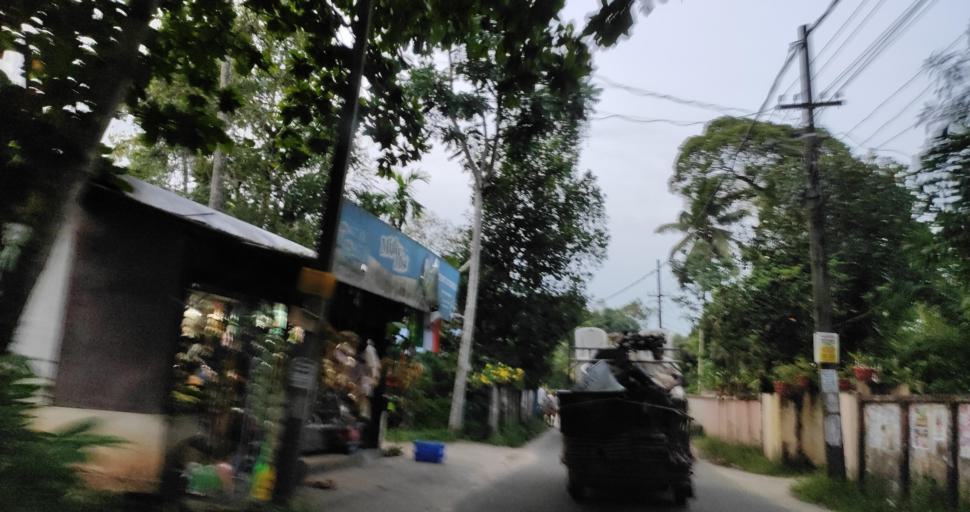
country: IN
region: Kerala
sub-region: Alappuzha
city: Vayalar
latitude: 9.6836
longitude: 76.3183
